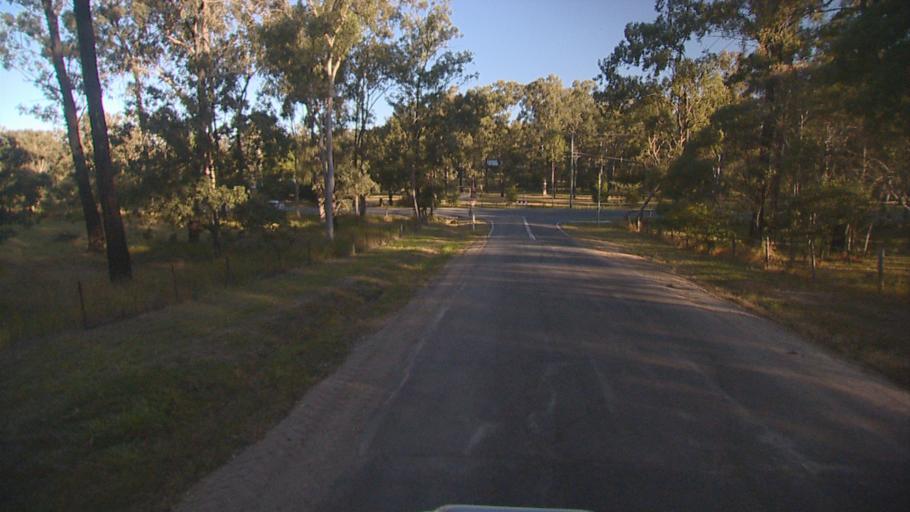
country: AU
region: Queensland
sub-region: Logan
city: Chambers Flat
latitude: -27.7680
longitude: 153.1274
